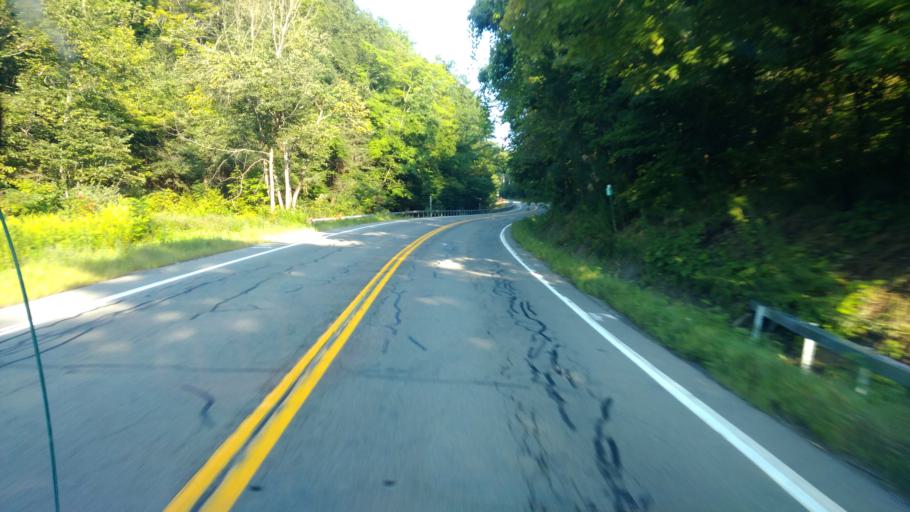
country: US
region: New York
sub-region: Allegany County
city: Andover
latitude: 42.1392
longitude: -77.6624
